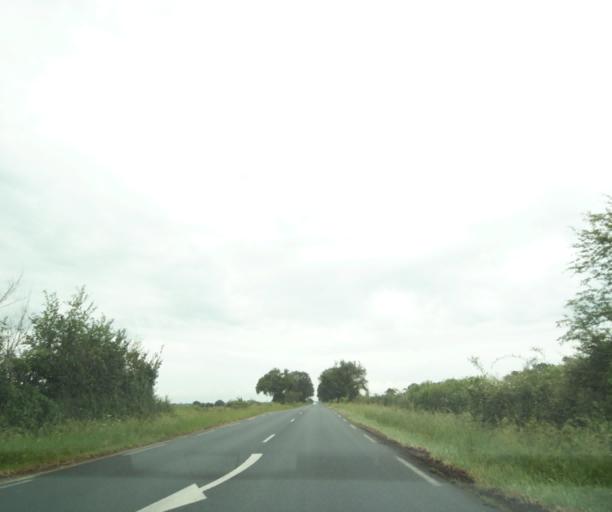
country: FR
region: Poitou-Charentes
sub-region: Departement des Deux-Sevres
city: Viennay
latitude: 46.7419
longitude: -0.2312
